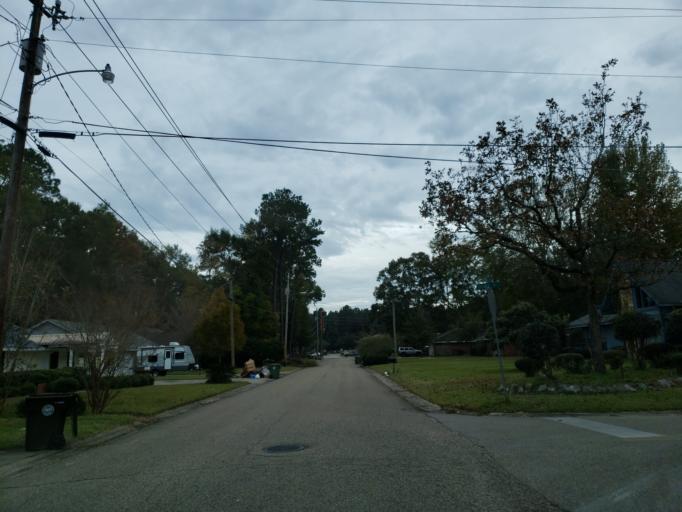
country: US
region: Mississippi
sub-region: Lamar County
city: West Hattiesburg
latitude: 31.3056
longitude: -89.3339
